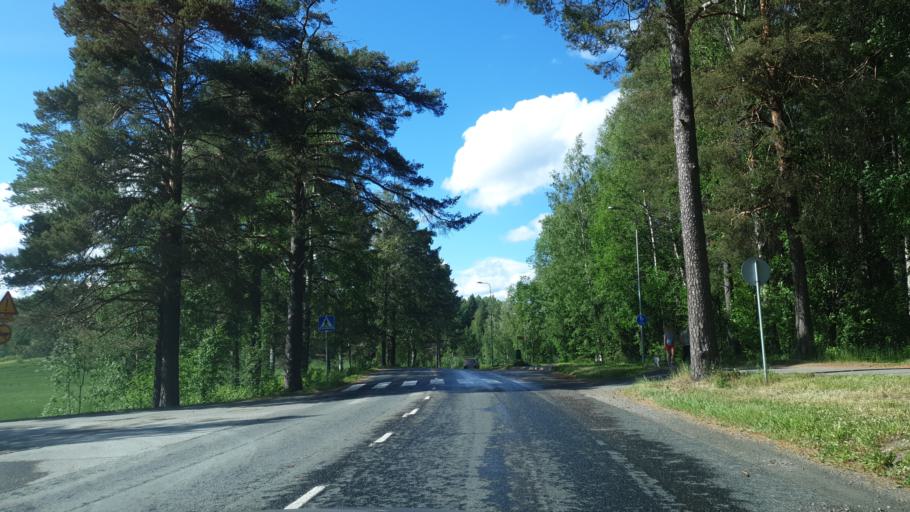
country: FI
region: Northern Savo
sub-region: Kuopio
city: Kuopio
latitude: 62.9174
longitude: 27.6310
